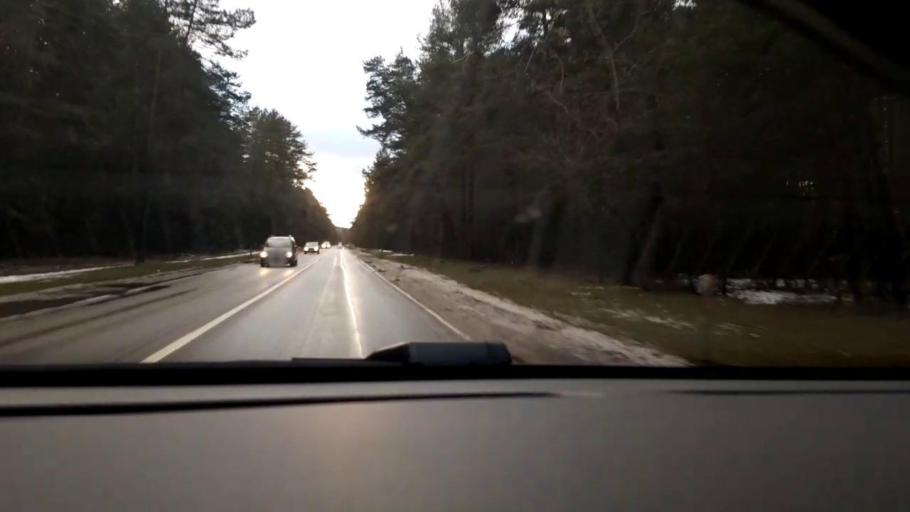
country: LT
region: Vilnius County
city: Rasos
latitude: 54.7695
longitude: 25.3800
